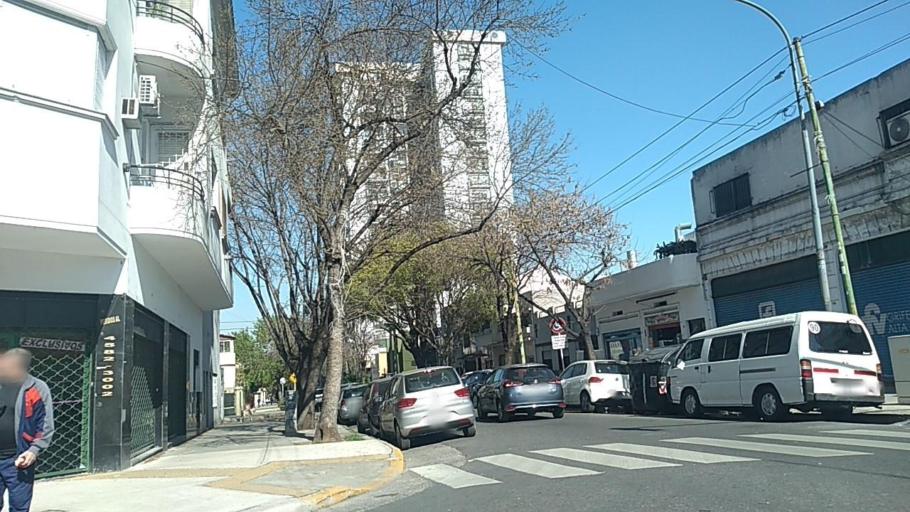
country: AR
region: Buenos Aires F.D.
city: Villa Santa Rita
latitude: -34.6100
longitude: -58.4879
